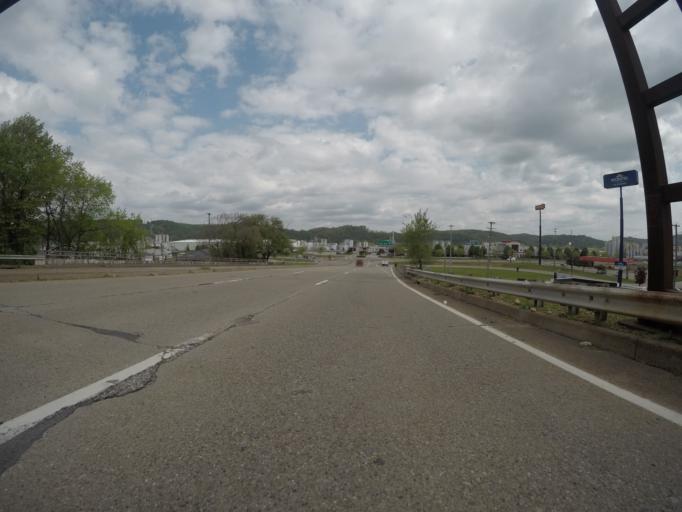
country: US
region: West Virginia
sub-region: Kanawha County
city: South Charleston
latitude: 38.3662
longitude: -81.6871
